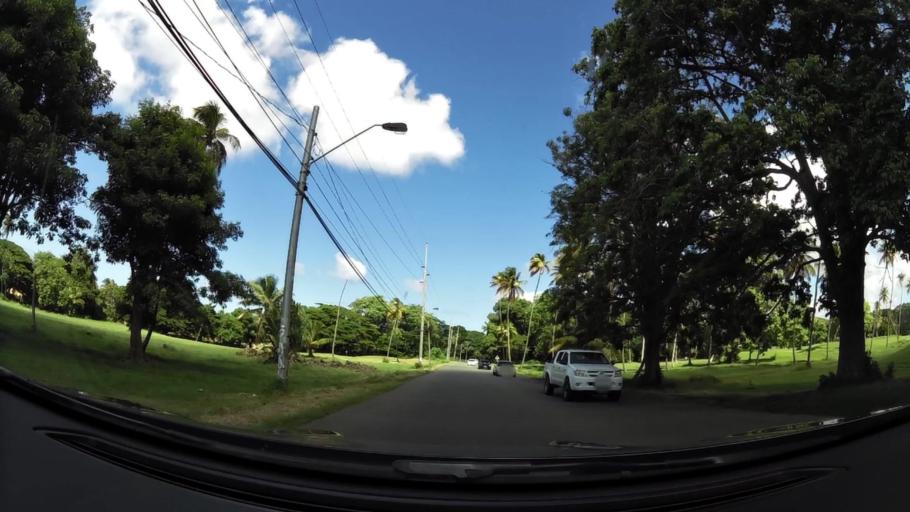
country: TT
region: Tobago
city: Scarborough
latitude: 11.1841
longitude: -60.7993
